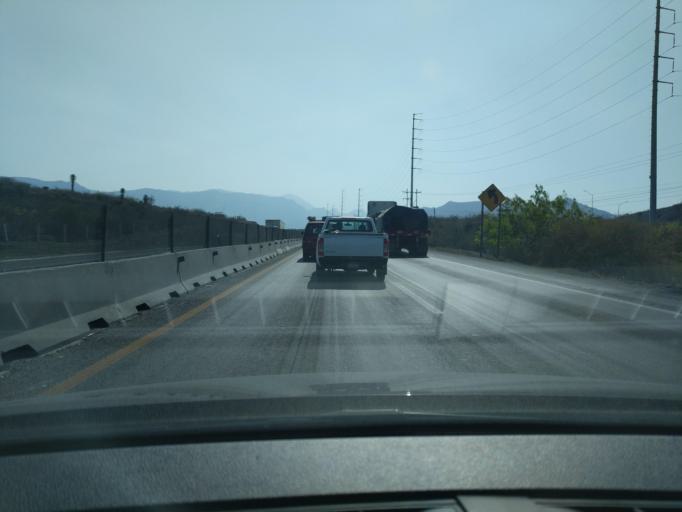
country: MX
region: Nuevo Leon
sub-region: Garcia
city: Los Parques
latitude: 25.7510
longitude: -100.5081
